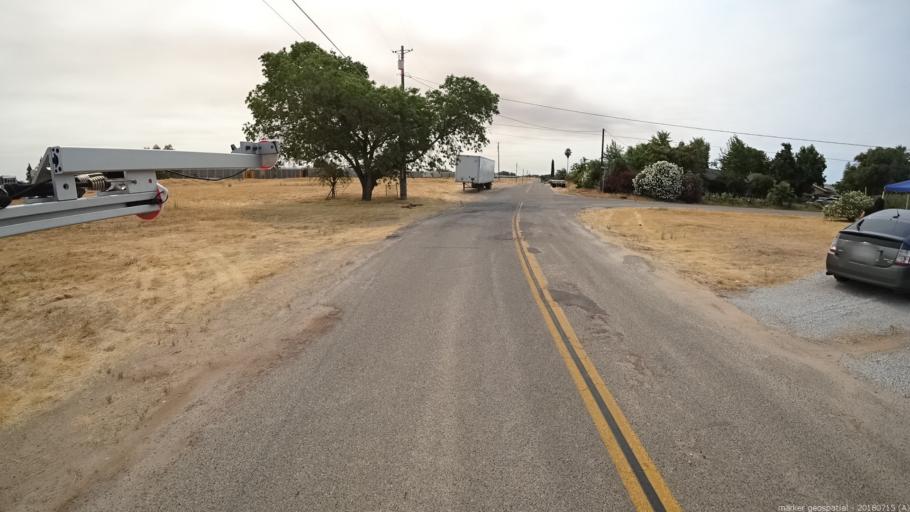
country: US
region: California
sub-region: Madera County
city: Madera Acres
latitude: 37.0172
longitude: -120.0702
